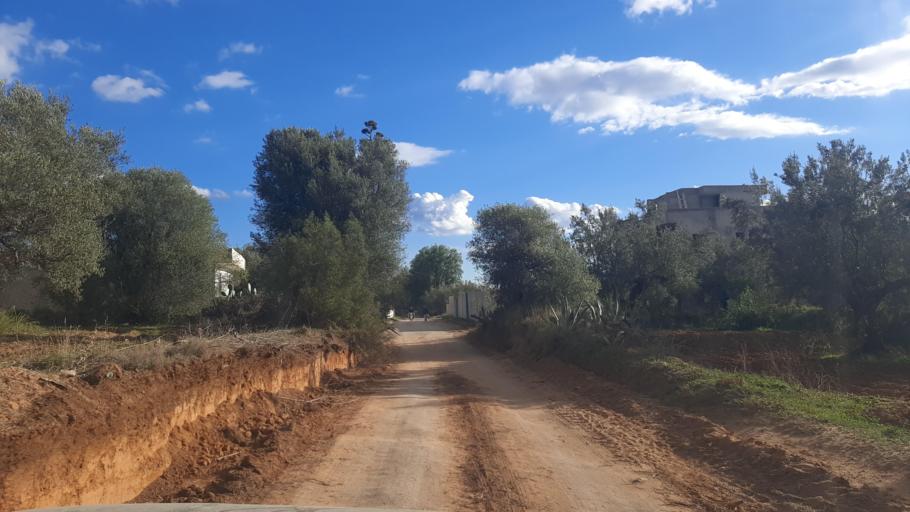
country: TN
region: Nabul
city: Al Hammamat
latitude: 36.4279
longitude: 10.5064
